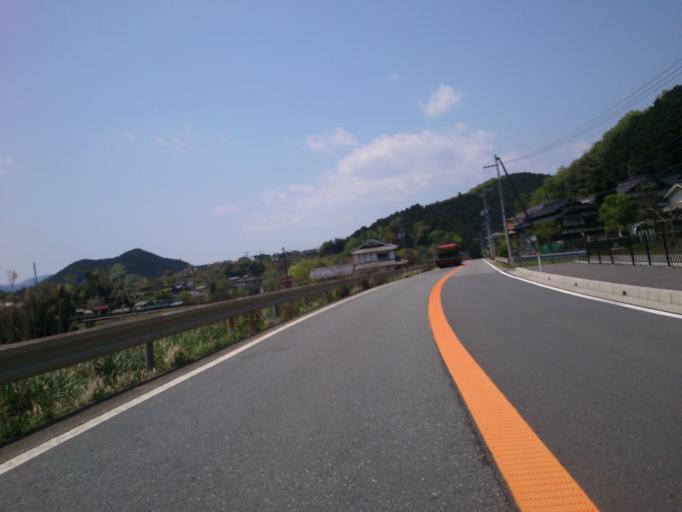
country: JP
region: Kyoto
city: Fukuchiyama
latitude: 35.3257
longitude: 135.0539
